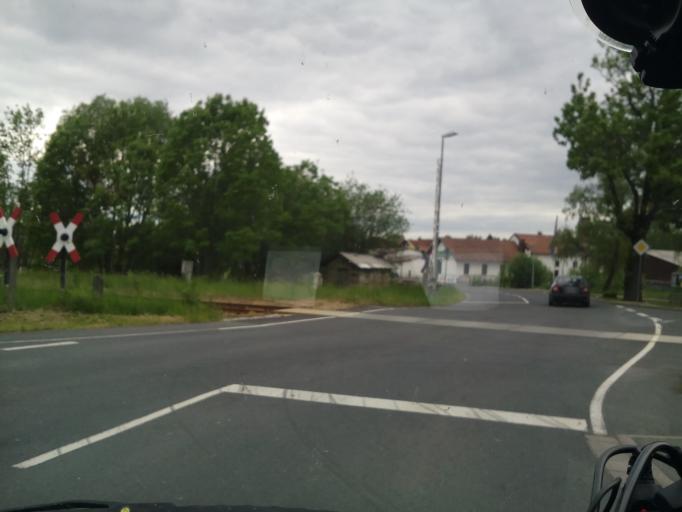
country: DE
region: Thuringia
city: Veilsdorf
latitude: 50.4146
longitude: 10.8089
